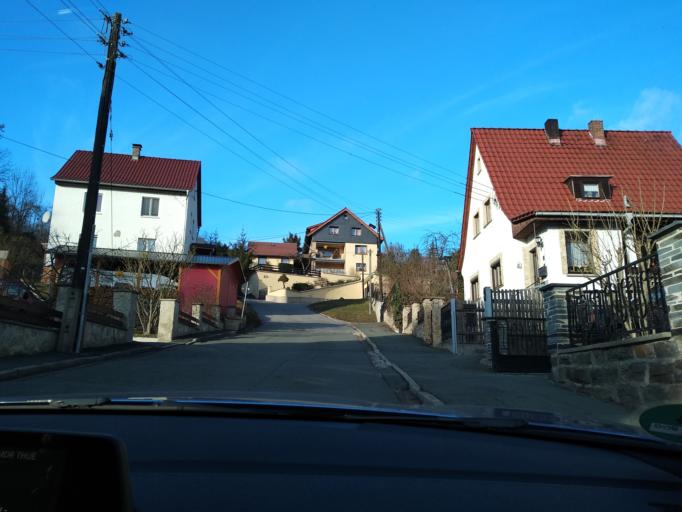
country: DE
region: Thuringia
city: Bad Blankenburg
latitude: 50.6870
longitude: 11.2593
